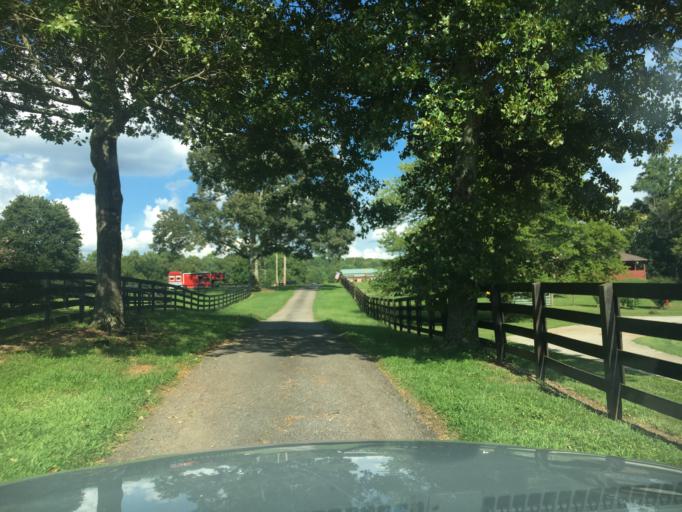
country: US
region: Georgia
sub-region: Cherokee County
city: Holly Springs
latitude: 34.1525
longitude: -84.4655
